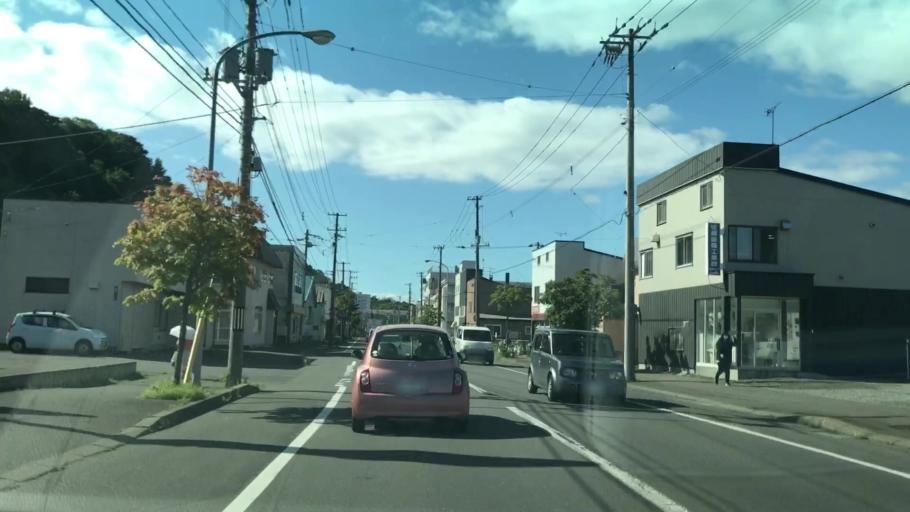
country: JP
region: Hokkaido
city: Muroran
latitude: 42.3337
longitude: 140.9618
